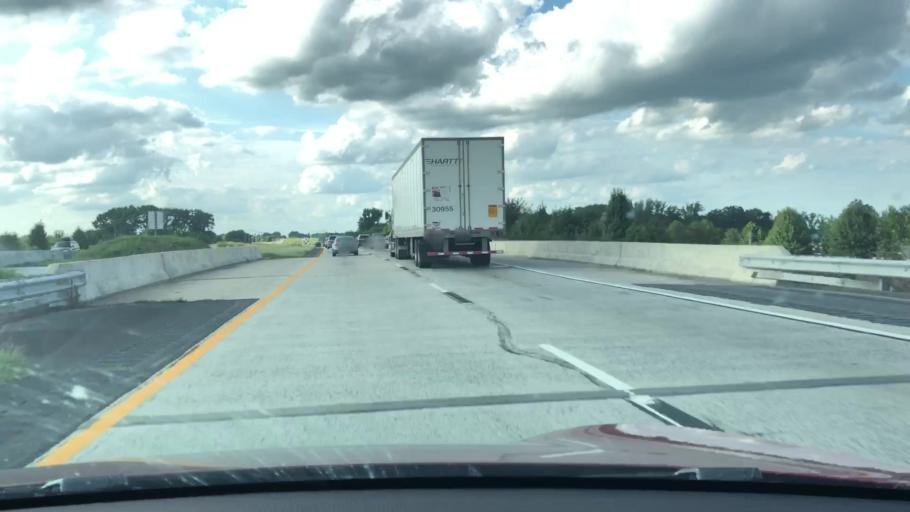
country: US
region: Delaware
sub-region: Kent County
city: Smyrna
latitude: 39.2725
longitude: -75.5820
